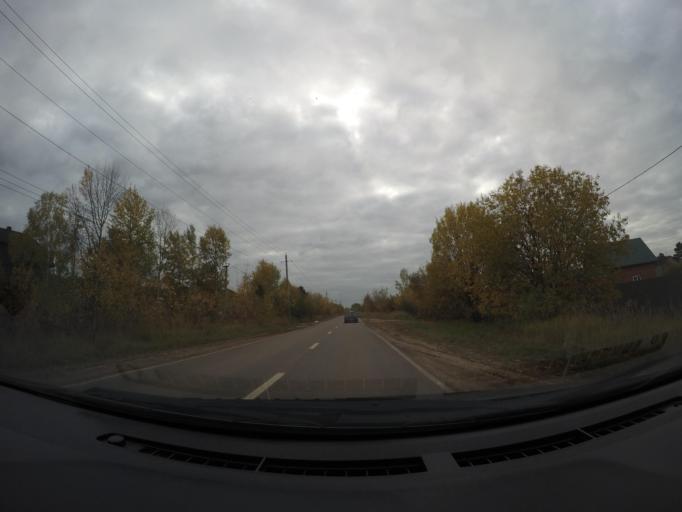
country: RU
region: Moskovskaya
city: Rechitsy
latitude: 55.6191
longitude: 38.4404
